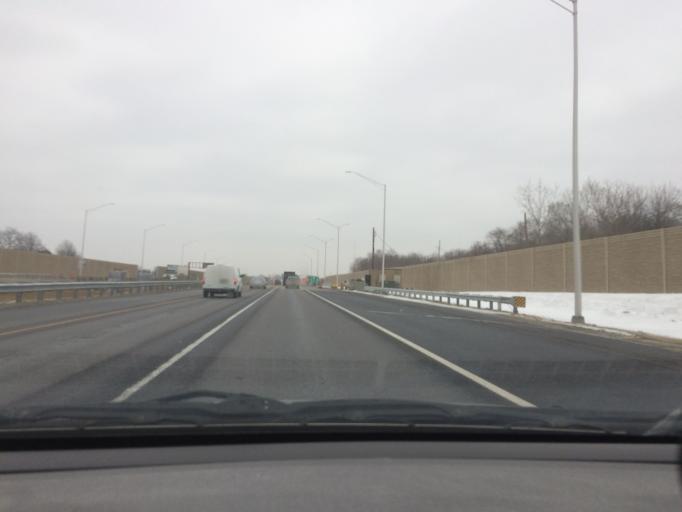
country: US
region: Illinois
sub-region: DuPage County
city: Roselle
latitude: 41.9921
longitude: -88.0592
